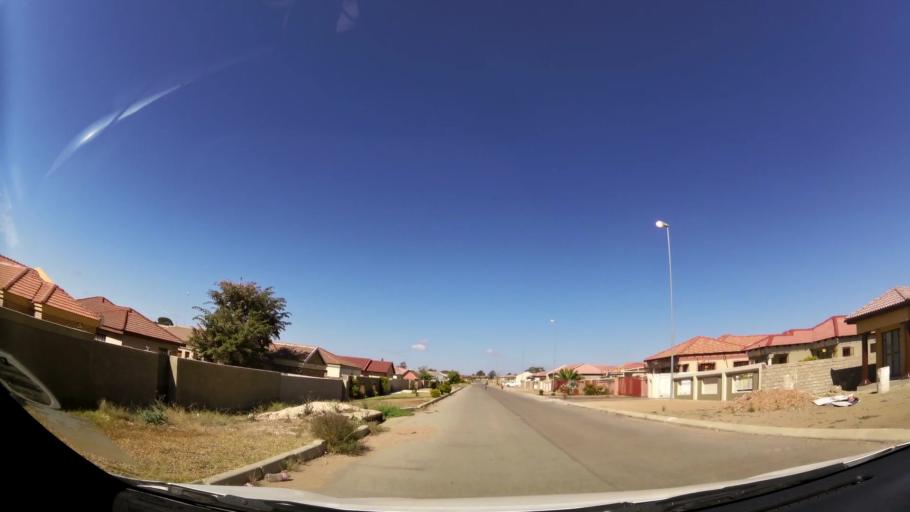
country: ZA
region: Limpopo
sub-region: Capricorn District Municipality
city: Polokwane
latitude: -23.8637
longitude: 29.4261
